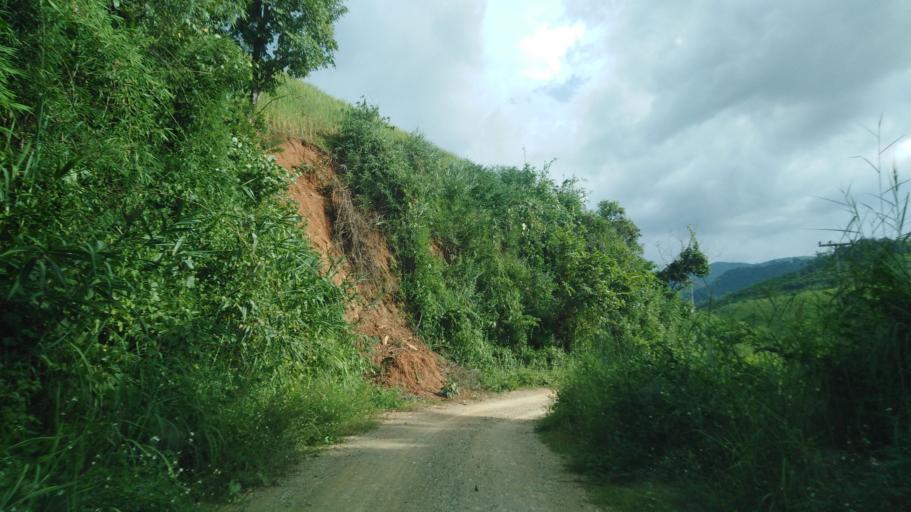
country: TH
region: Chiang Rai
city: Wiang Kaen
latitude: 19.7801
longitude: 100.6527
